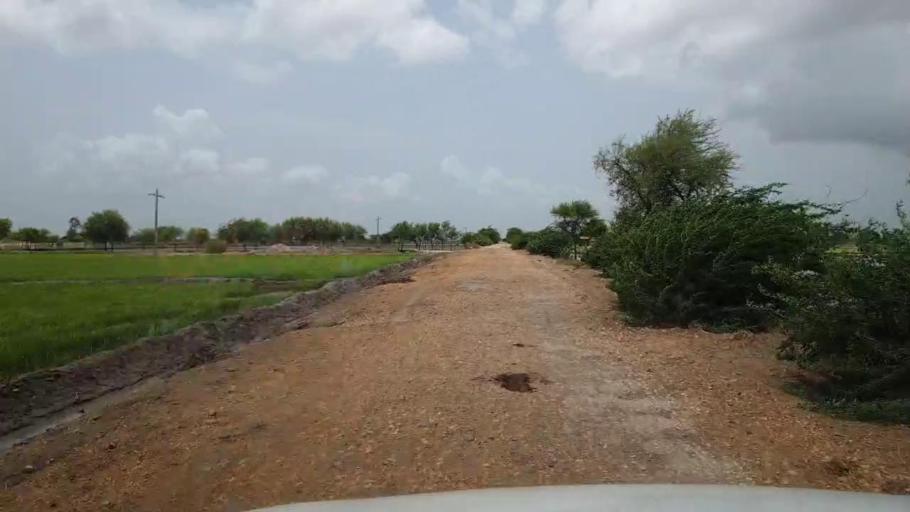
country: PK
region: Sindh
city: Kario
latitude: 24.7555
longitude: 68.4577
